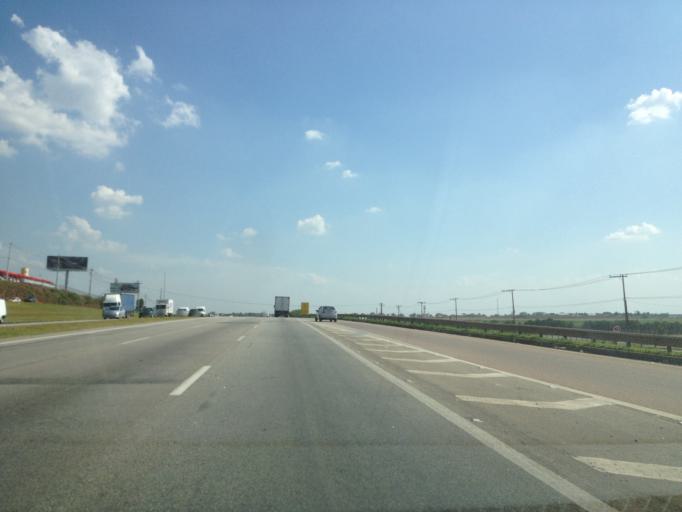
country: BR
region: Sao Paulo
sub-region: Campinas
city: Campinas
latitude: -23.0086
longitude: -47.1148
